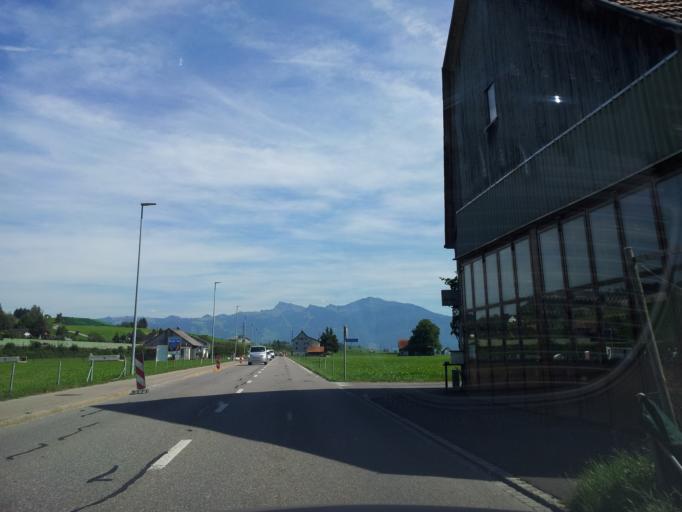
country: CH
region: Schwyz
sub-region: Bezirk March
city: Schubelbach
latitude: 47.1912
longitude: 8.8981
